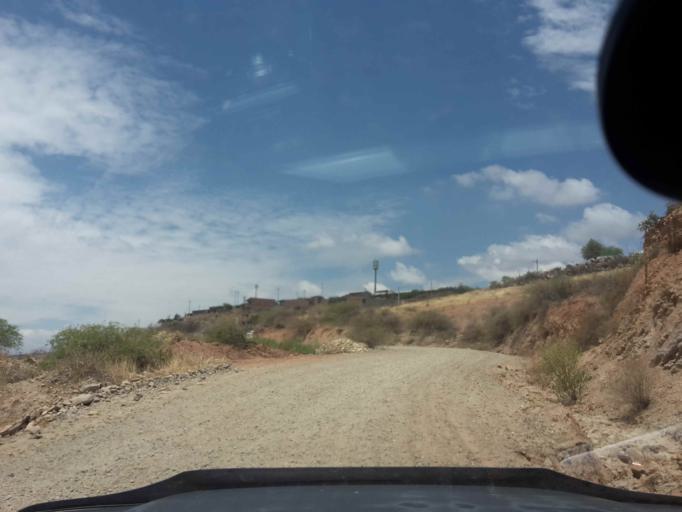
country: BO
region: Cochabamba
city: Sipe Sipe
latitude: -17.5652
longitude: -66.3495
